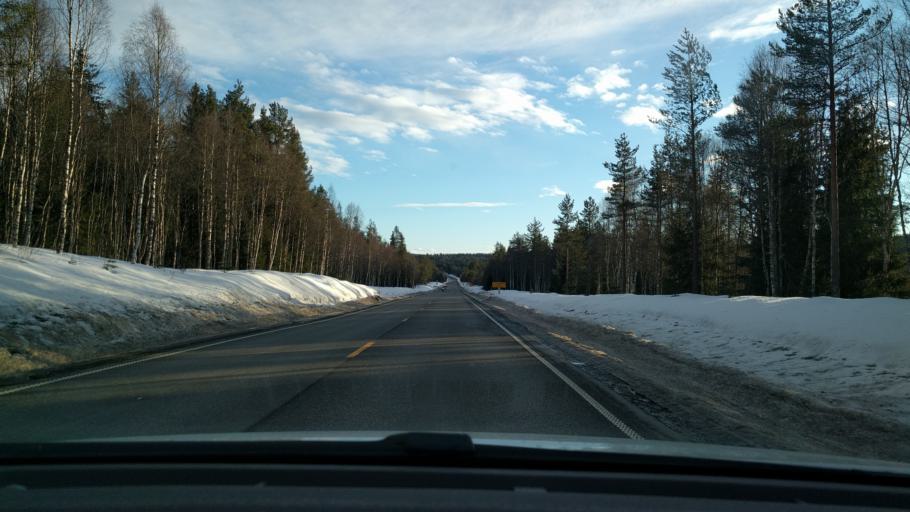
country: NO
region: Hedmark
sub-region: Elverum
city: Elverum
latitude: 61.0368
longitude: 11.8694
